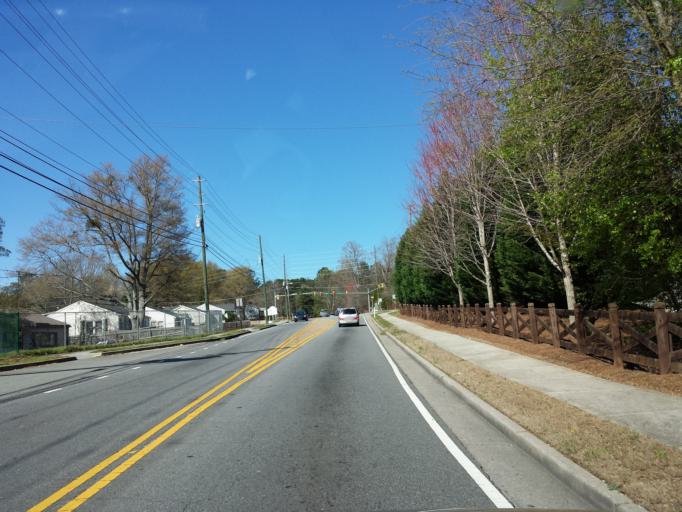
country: US
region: Georgia
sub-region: Cobb County
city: Fair Oaks
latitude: 33.9221
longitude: -84.5559
